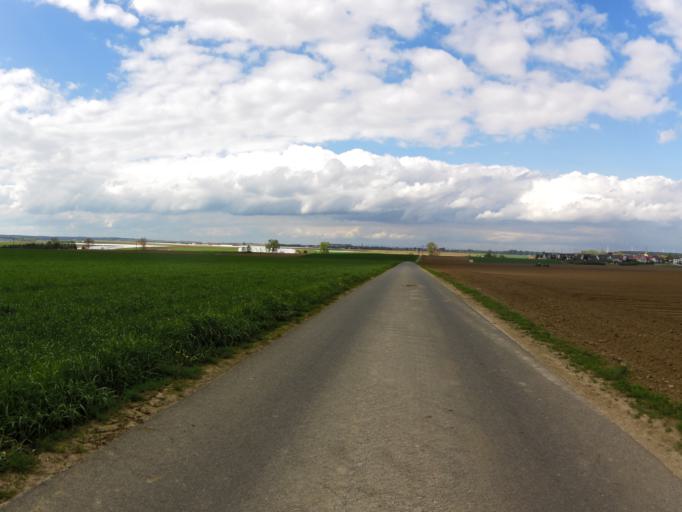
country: DE
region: Bavaria
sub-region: Regierungsbezirk Unterfranken
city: Oberpleichfeld
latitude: 49.8695
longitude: 10.0798
